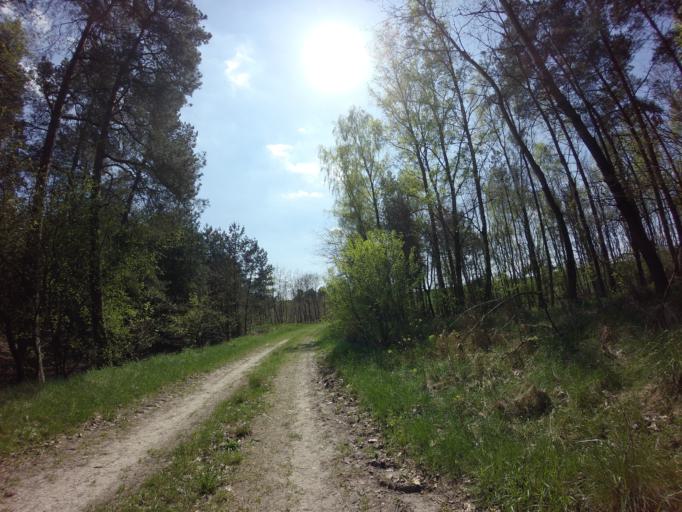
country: PL
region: West Pomeranian Voivodeship
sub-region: Powiat stargardzki
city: Suchan
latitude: 53.2157
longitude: 15.3025
